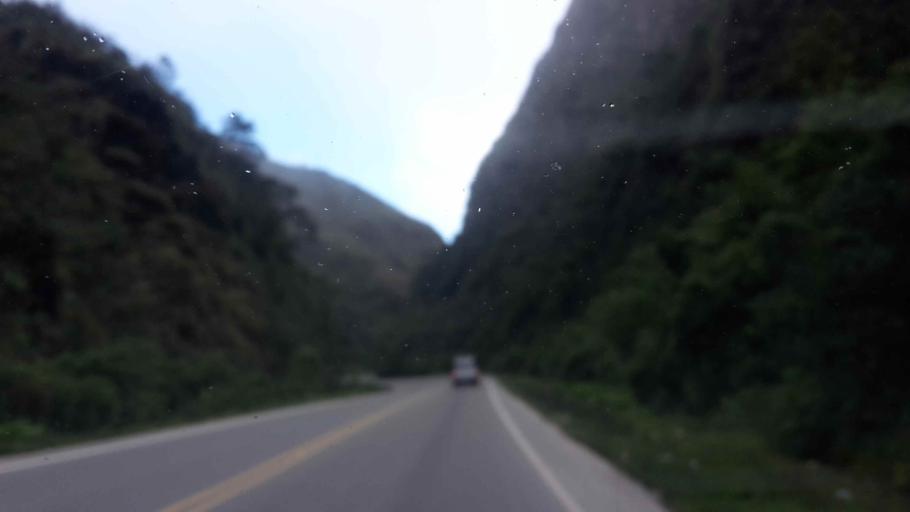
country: BO
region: Cochabamba
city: Colomi
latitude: -17.2090
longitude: -65.8888
